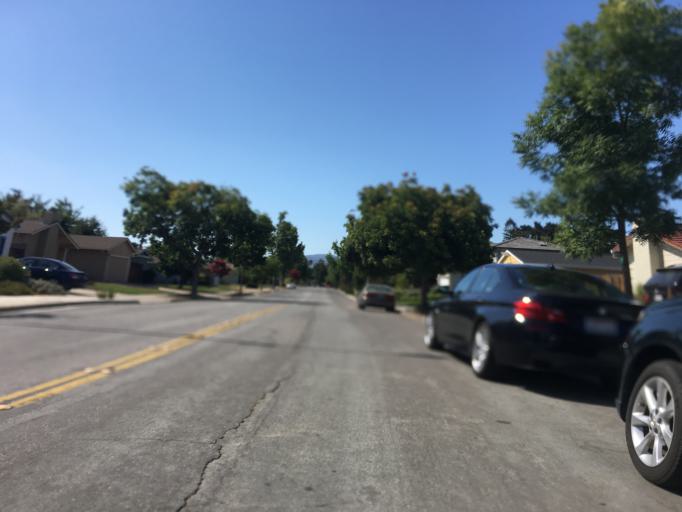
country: US
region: California
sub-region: Santa Clara County
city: Cupertino
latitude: 37.3292
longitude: -122.0241
